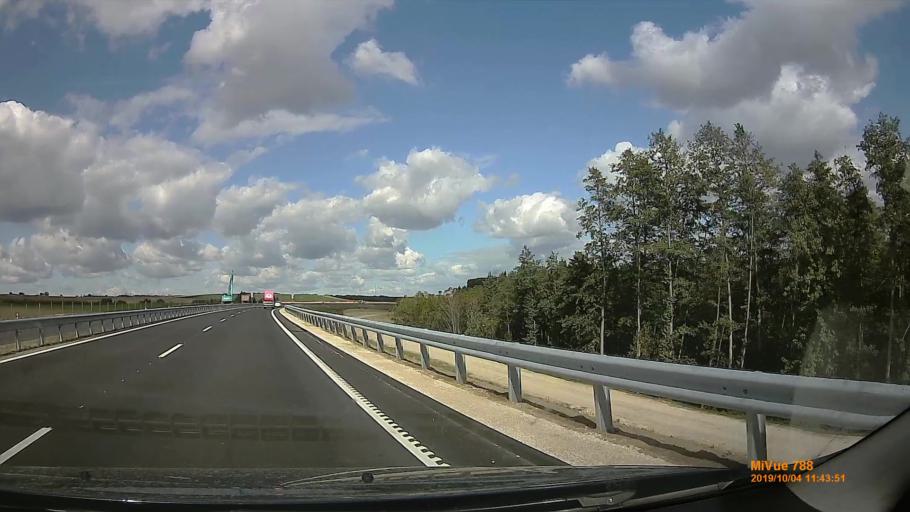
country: HU
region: Somogy
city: Karad
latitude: 46.6060
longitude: 17.7997
